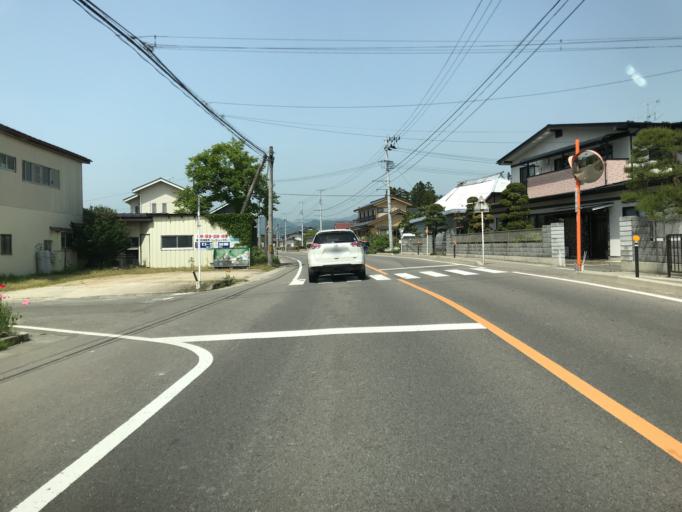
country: JP
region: Fukushima
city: Hobaramachi
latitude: 37.8249
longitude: 140.4767
